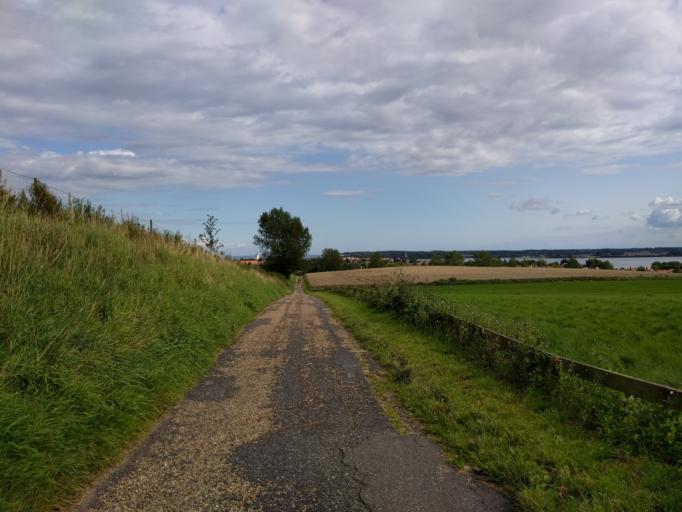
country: DK
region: South Denmark
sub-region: Kerteminde Kommune
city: Kerteminde
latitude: 55.4606
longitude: 10.6274
